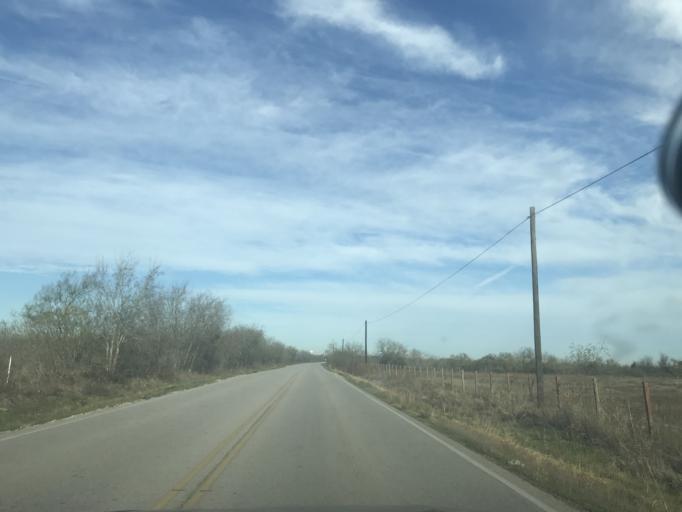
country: US
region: Texas
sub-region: Travis County
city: Manor
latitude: 30.2953
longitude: -97.5248
